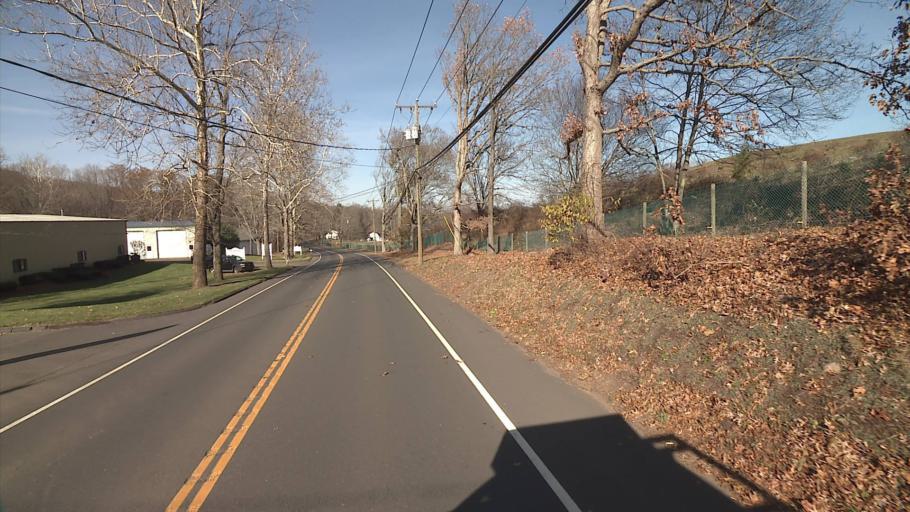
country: US
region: Connecticut
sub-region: Middlesex County
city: Portland
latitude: 41.5782
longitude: -72.6074
